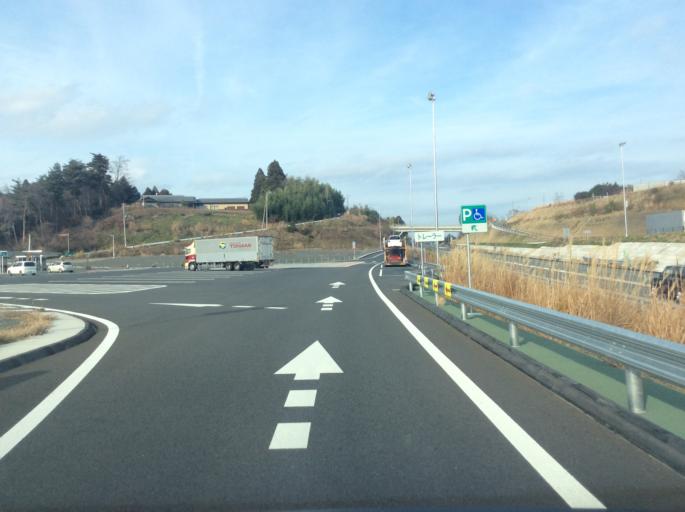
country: JP
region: Fukushima
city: Namie
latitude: 37.2864
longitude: 140.9813
